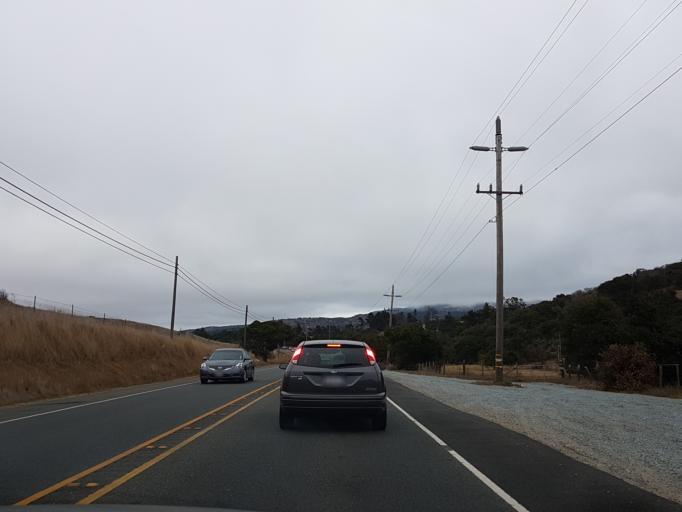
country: US
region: California
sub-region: Monterey County
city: Carmel Valley Village
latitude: 36.5722
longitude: -121.7415
